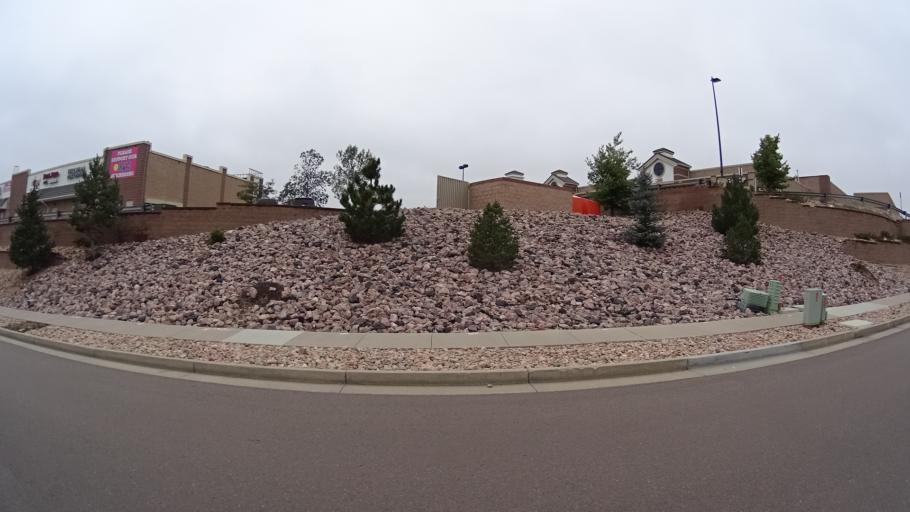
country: US
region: Colorado
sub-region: El Paso County
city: Cimarron Hills
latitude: 38.9116
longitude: -104.7148
